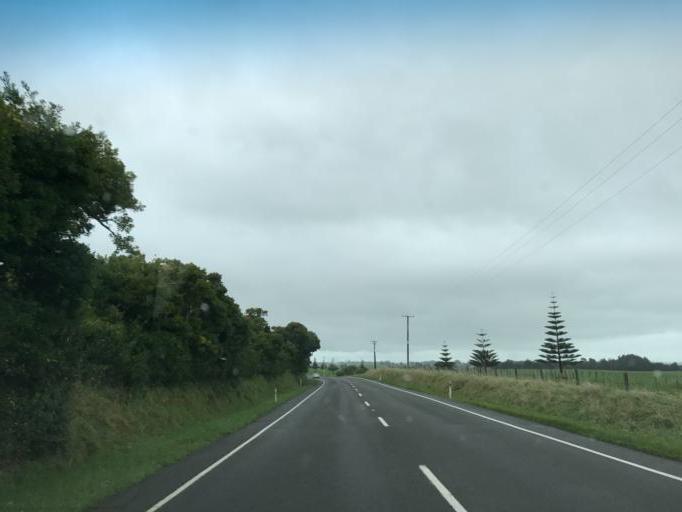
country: NZ
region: Manawatu-Wanganui
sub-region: Wanganui District
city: Wanganui
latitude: -39.8151
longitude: 174.8078
